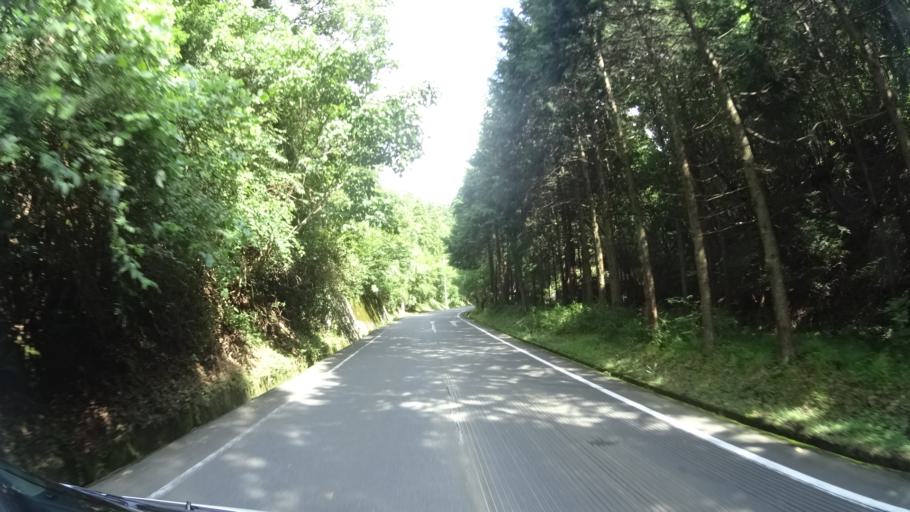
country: JP
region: Kyoto
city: Fukuchiyama
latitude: 35.3464
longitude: 135.1549
